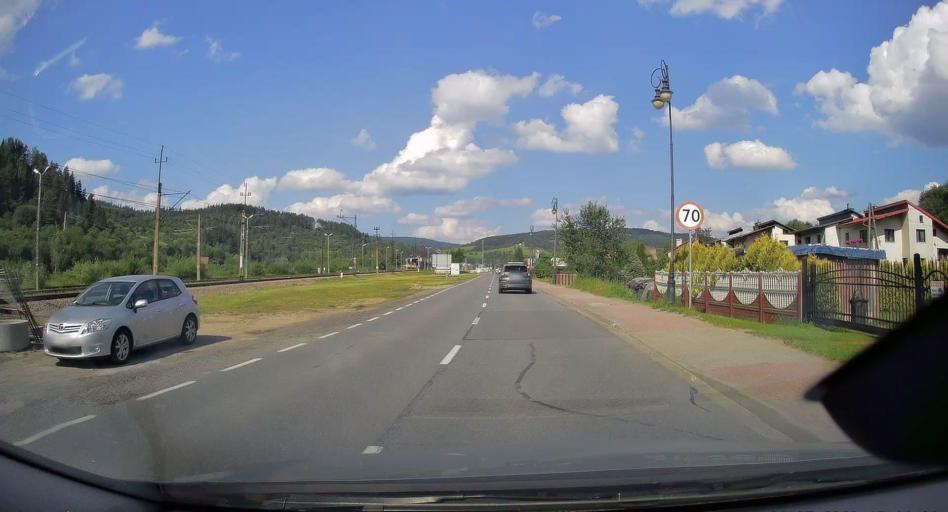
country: PL
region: Lesser Poland Voivodeship
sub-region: Powiat nowosadecki
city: Muszyna
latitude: 49.3656
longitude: 20.9347
